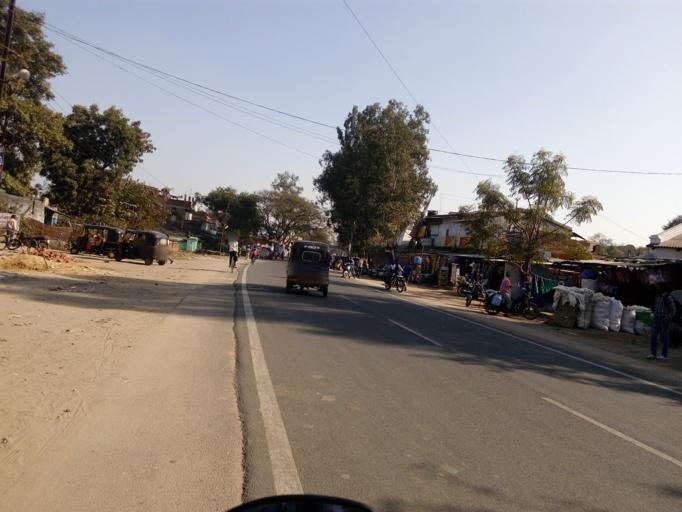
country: IN
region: Jharkhand
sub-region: Ranchi
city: Ranchi
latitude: 23.3583
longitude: 85.3612
